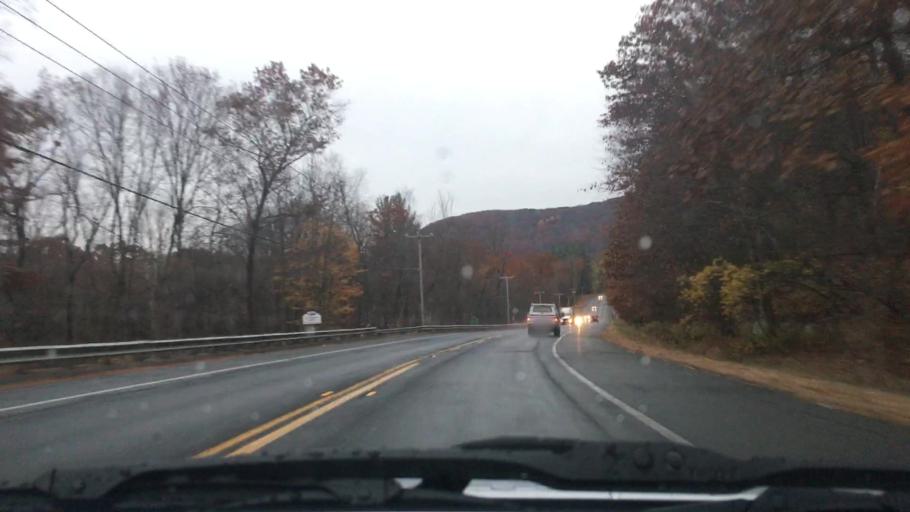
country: US
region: Massachusetts
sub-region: Hampden County
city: Westfield
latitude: 42.1749
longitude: -72.8328
